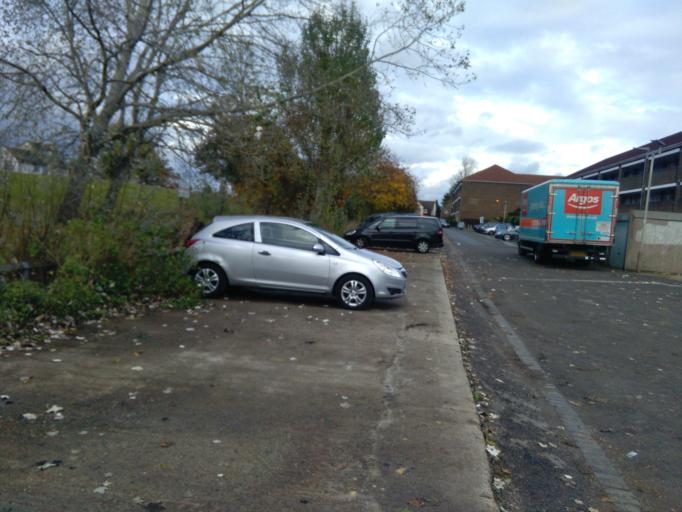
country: GB
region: England
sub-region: Greater London
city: Feltham
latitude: 51.4470
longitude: -0.4298
